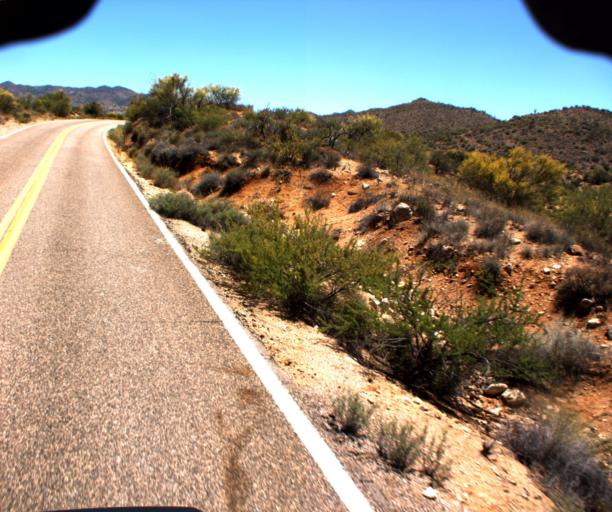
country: US
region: Arizona
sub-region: Yavapai County
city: Bagdad
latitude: 34.4698
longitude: -113.0510
